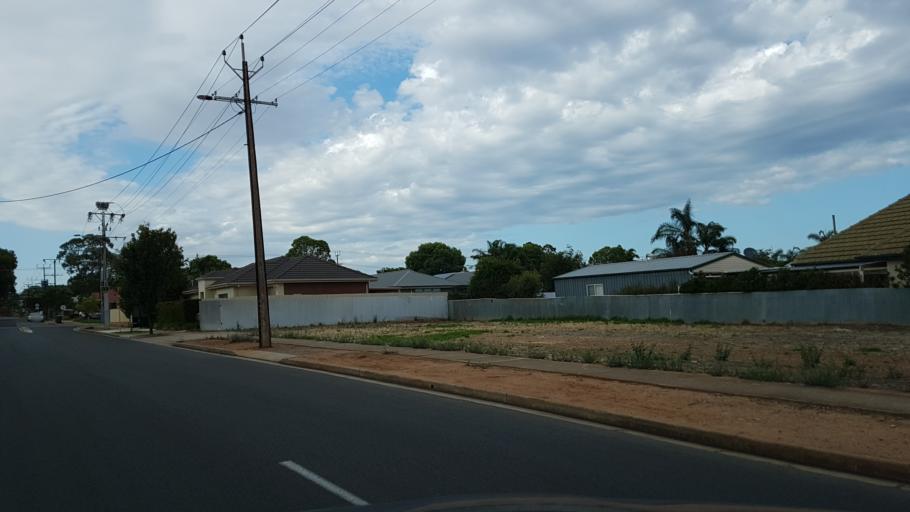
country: AU
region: South Australia
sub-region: Marion
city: Clovelly Park
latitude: -34.9991
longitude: 138.5691
